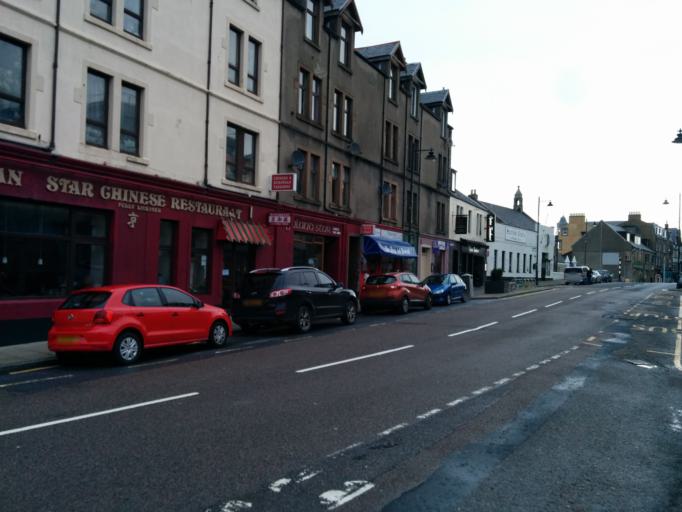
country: GB
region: Scotland
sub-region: Highland
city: Fort William
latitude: 56.8157
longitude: -5.1152
